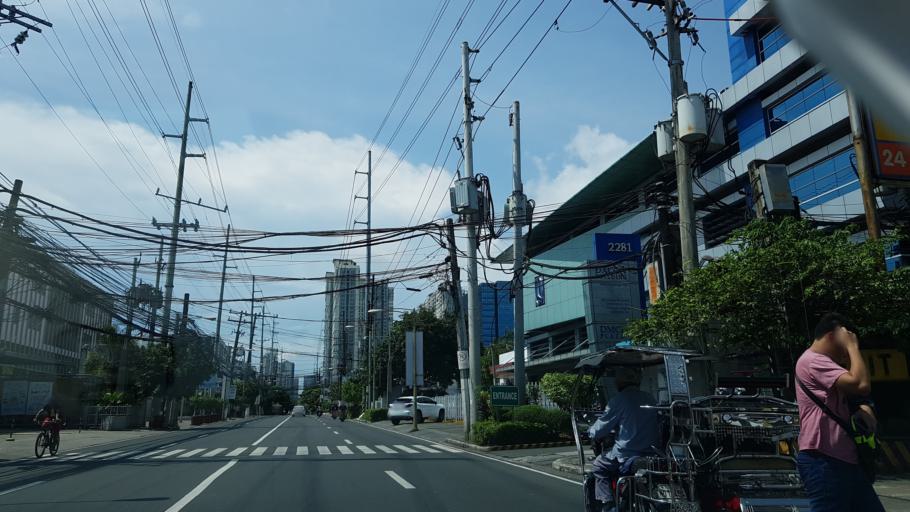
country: PH
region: Metro Manila
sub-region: Makati City
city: Makati City
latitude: 14.5373
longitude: 121.0205
